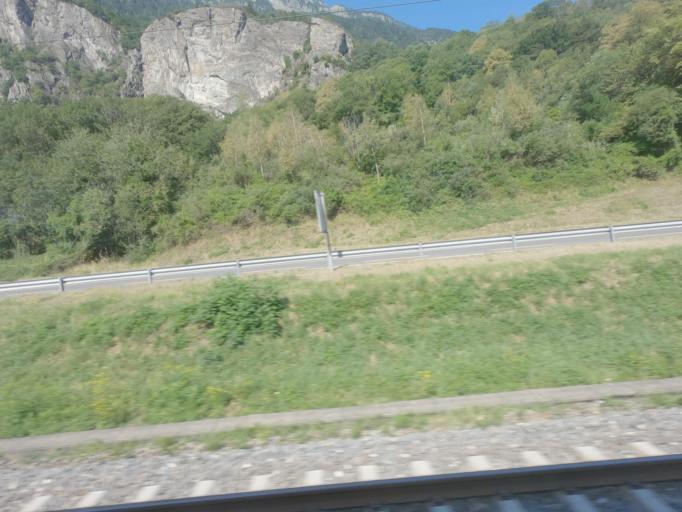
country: CH
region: Valais
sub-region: Saint-Maurice District
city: Vernayaz
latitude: 46.1520
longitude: 7.0311
